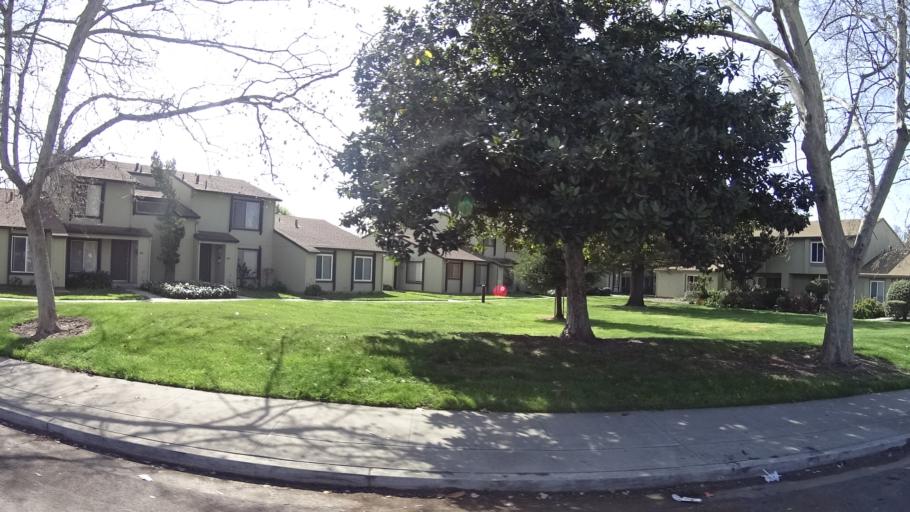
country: US
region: California
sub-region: Santa Clara County
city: Alum Rock
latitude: 37.3814
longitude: -121.8691
